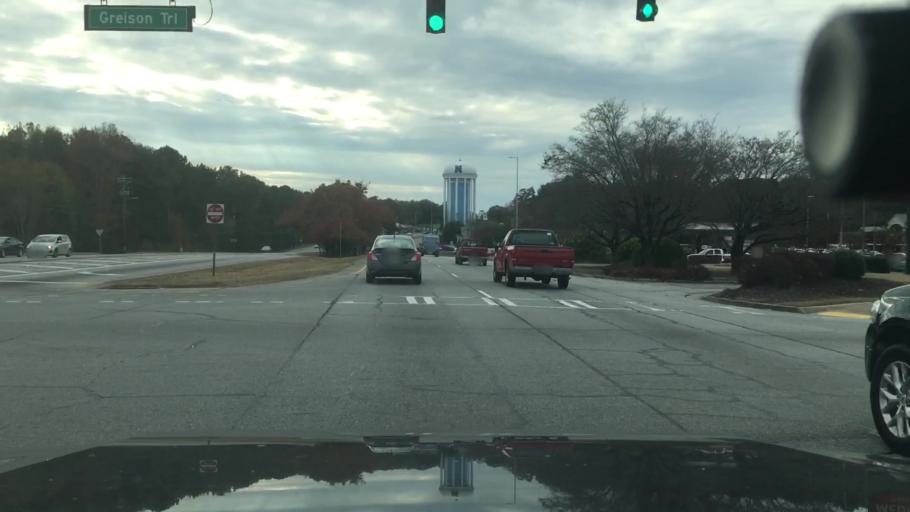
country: US
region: Georgia
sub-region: Coweta County
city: Newnan
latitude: 33.3847
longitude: -84.7842
